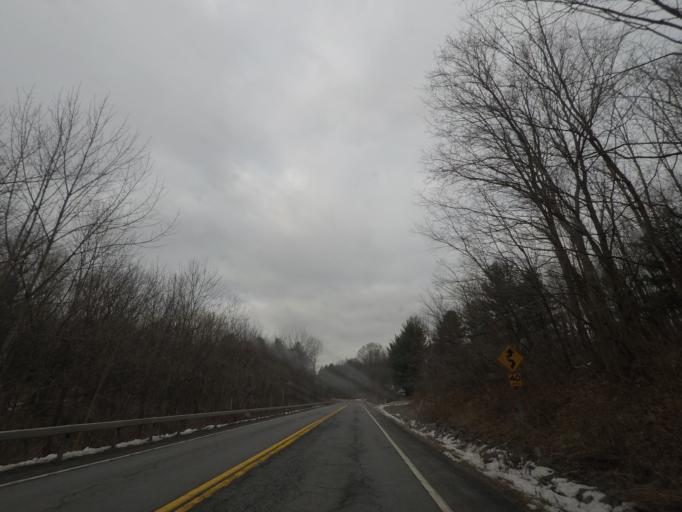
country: US
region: New York
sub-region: Rensselaer County
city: West Sand Lake
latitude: 42.6116
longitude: -73.6268
